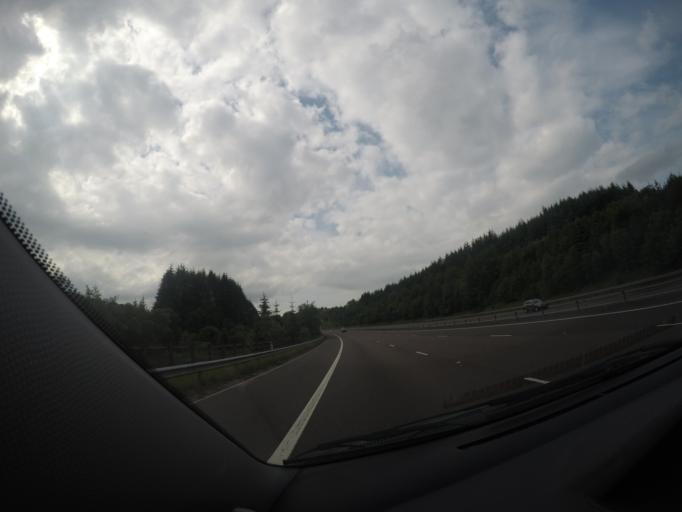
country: GB
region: Scotland
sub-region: Dumfries and Galloway
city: Moffat
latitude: 55.4057
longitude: -3.5578
